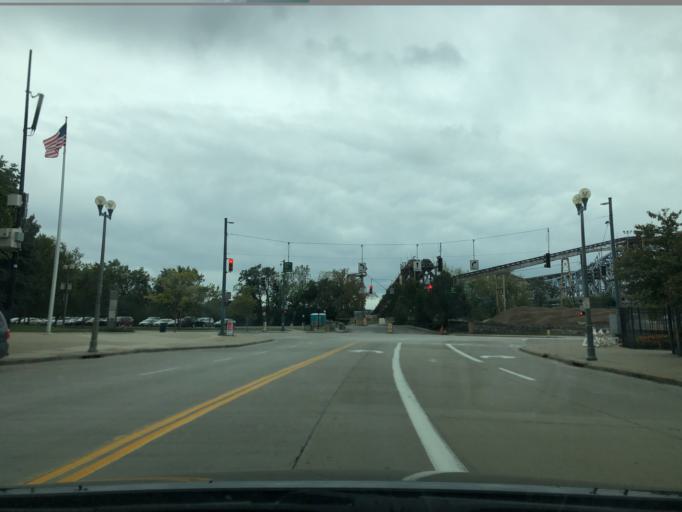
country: US
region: Kentucky
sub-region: Kenton County
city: Covington
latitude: 39.0948
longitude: -84.5180
